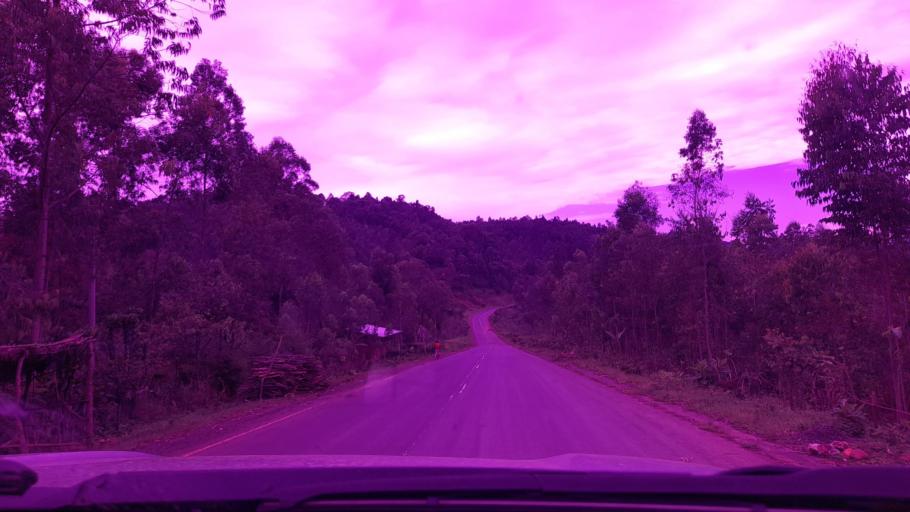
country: ET
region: Southern Nations, Nationalities, and People's Region
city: Mizan Teferi
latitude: 7.0616
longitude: 35.6266
